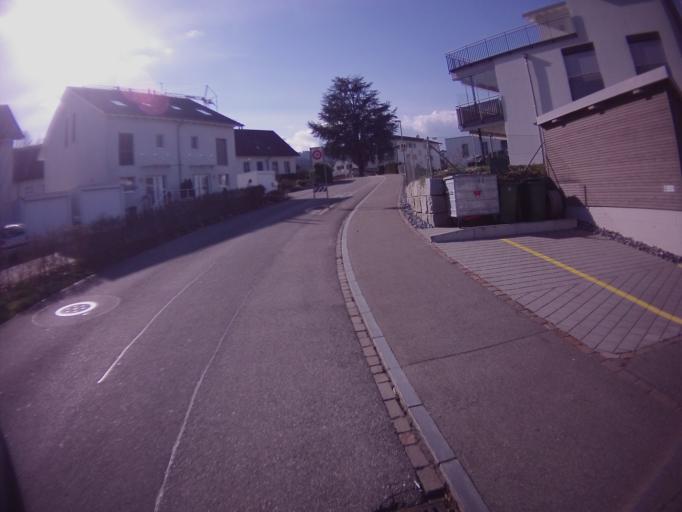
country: CH
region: Aargau
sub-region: Bezirk Baden
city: Killwangen
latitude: 47.4309
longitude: 8.3544
